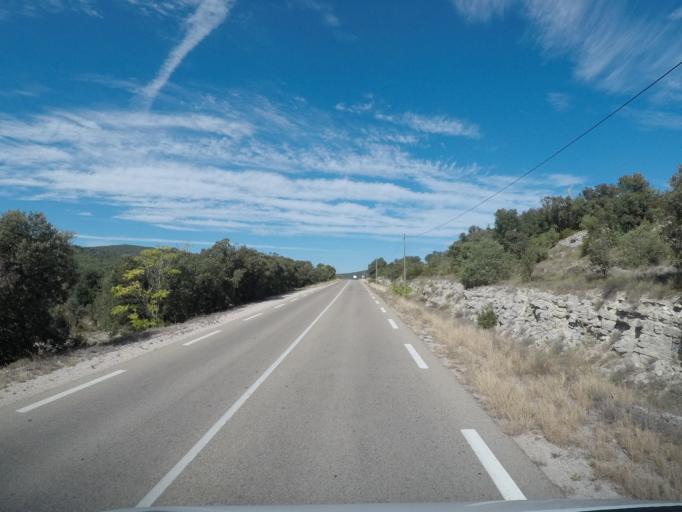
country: FR
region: Languedoc-Roussillon
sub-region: Departement de l'Herault
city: Saint-Martin-de-Londres
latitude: 43.8208
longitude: 3.7446
